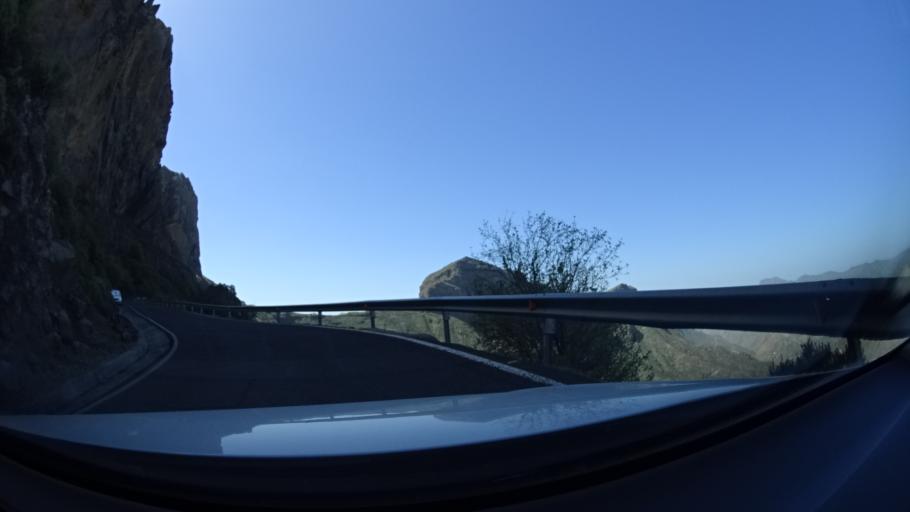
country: ES
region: Canary Islands
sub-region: Provincia de Las Palmas
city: Tejeda
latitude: 27.9681
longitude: -15.6243
